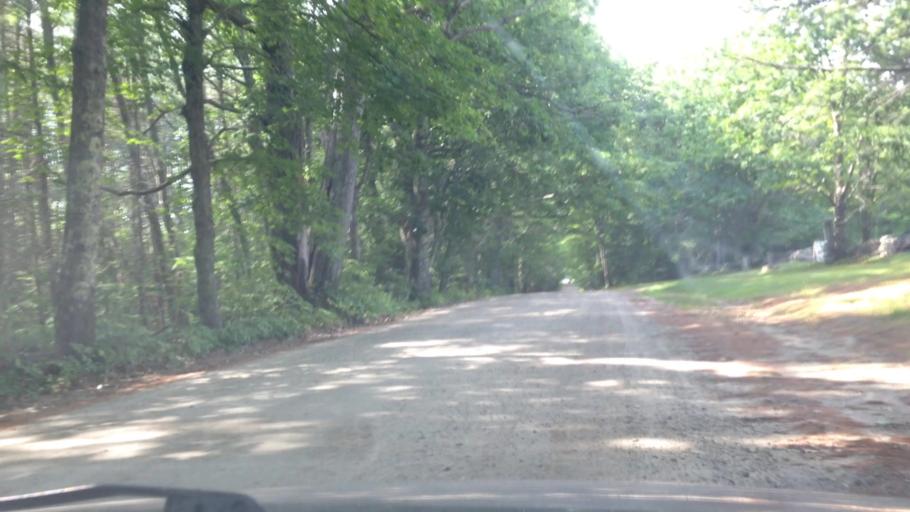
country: US
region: New Hampshire
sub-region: Cheshire County
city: Marlborough
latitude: 42.8851
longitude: -72.1897
